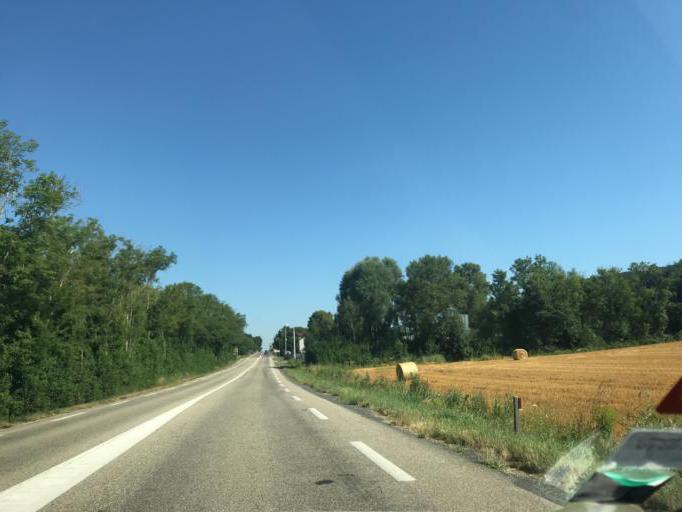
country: FR
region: Rhone-Alpes
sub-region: Departement de l'Ain
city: Saint-Martin-du-Mont
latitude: 46.0783
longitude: 5.3212
